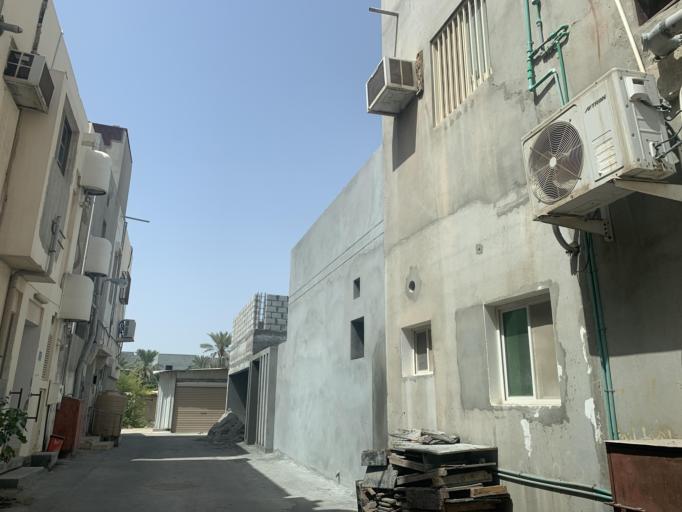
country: BH
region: Central Governorate
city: Madinat Hamad
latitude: 26.1467
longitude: 50.4964
